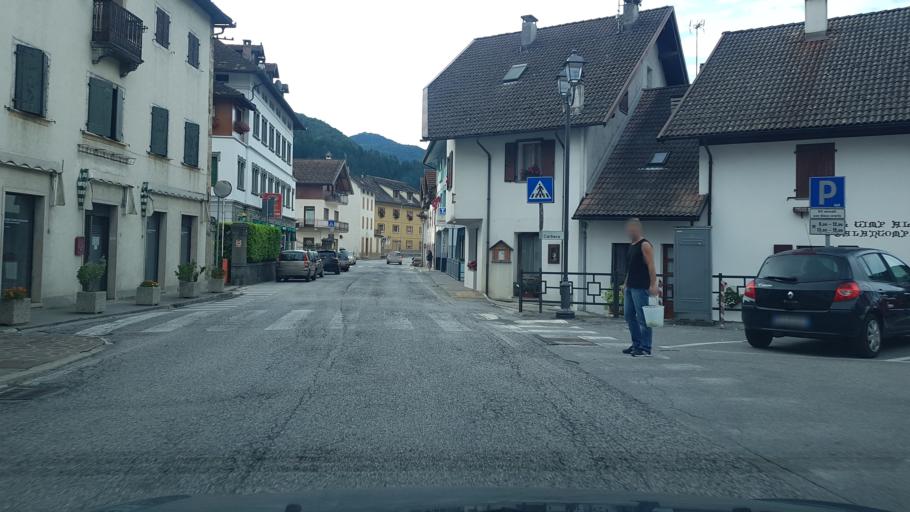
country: IT
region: Friuli Venezia Giulia
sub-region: Provincia di Udine
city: Ovaro
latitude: 46.4821
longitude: 12.8660
